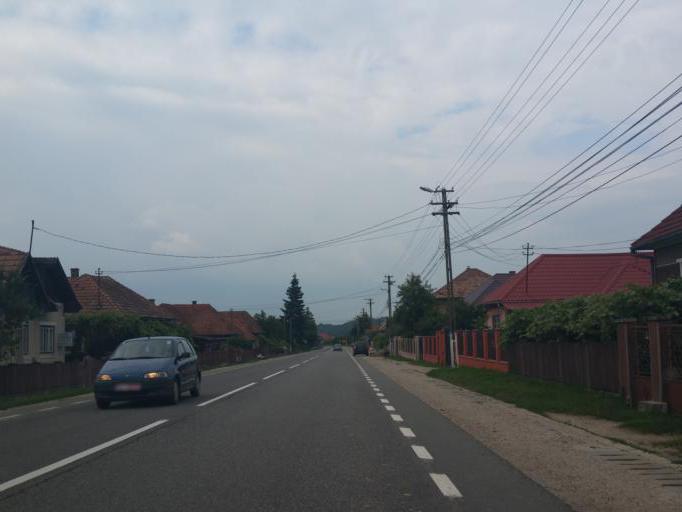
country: RO
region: Salaj
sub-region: Comuna Romanasi
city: Romanasi
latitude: 47.0879
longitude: 23.1898
